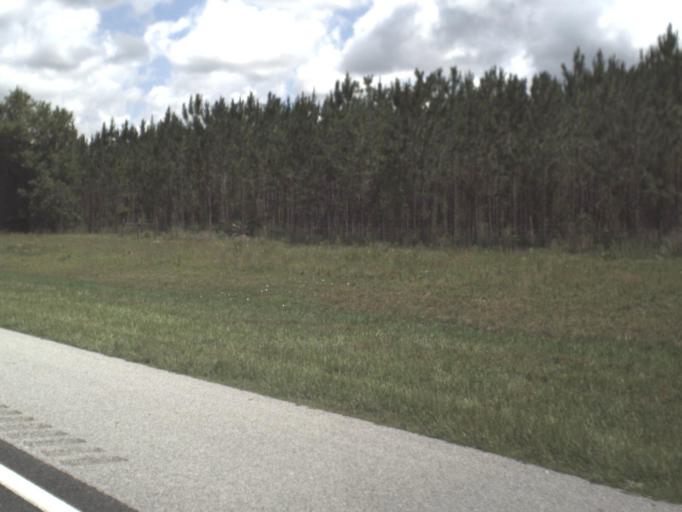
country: US
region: Florida
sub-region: Suwannee County
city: Wellborn
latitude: 30.3263
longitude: -82.8165
